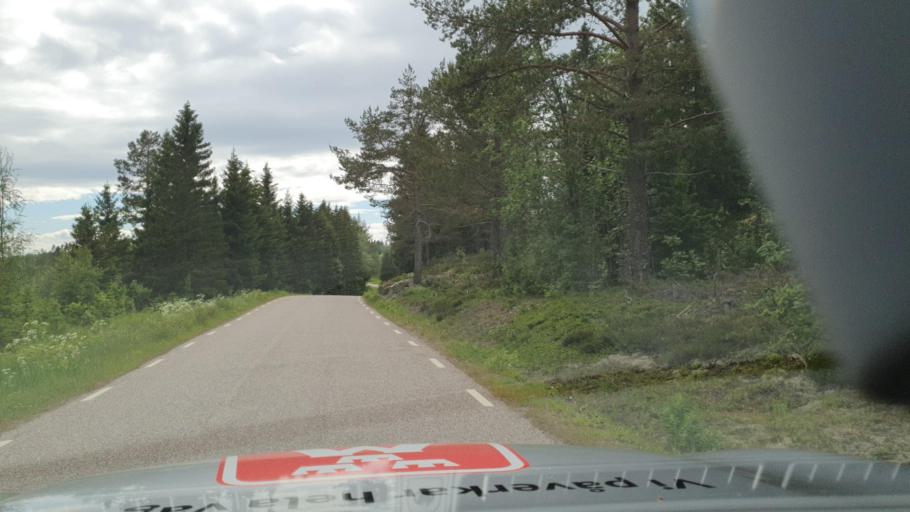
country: SE
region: Vaesternorrland
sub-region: Kramfors Kommun
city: Nordingra
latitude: 62.8666
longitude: 18.3679
